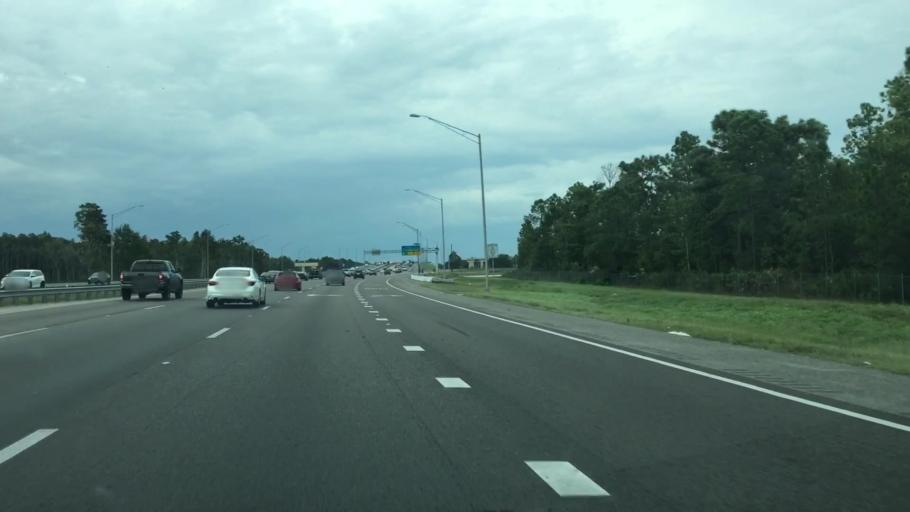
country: US
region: Florida
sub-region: Orange County
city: Azalea Park
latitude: 28.4705
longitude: -81.2374
